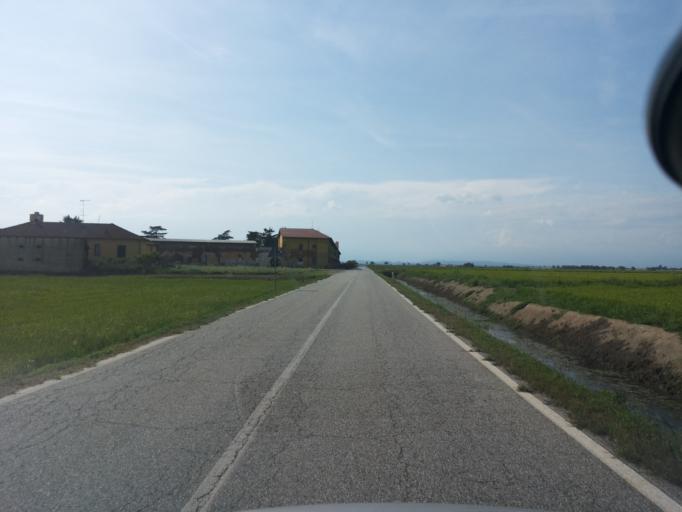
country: IT
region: Piedmont
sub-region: Provincia di Vercelli
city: Sali Vercellese
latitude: 45.2919
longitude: 8.2935
